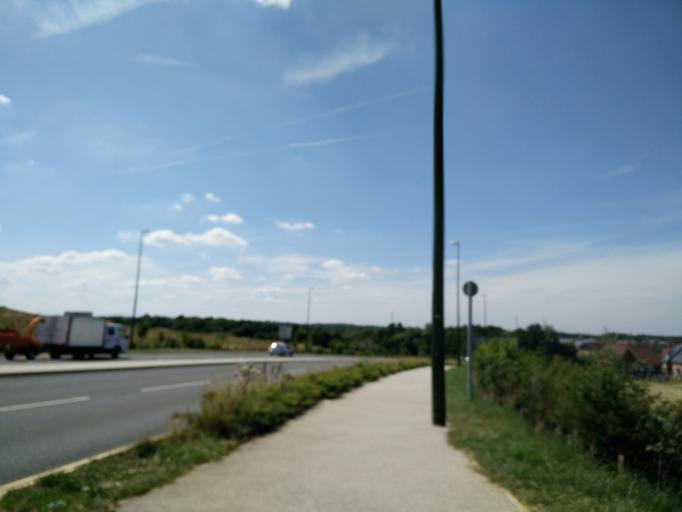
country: GB
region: England
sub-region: West Sussex
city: Horsham
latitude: 51.0617
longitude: -0.3593
